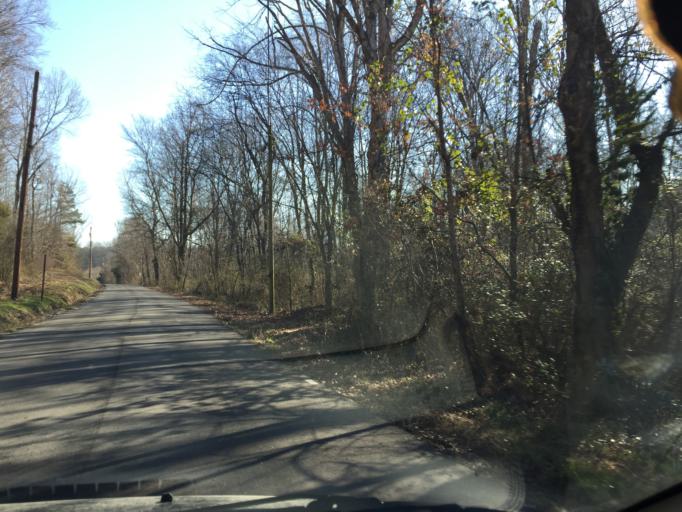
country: US
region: Tennessee
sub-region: Hamilton County
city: Collegedale
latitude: 35.0793
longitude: -85.0855
